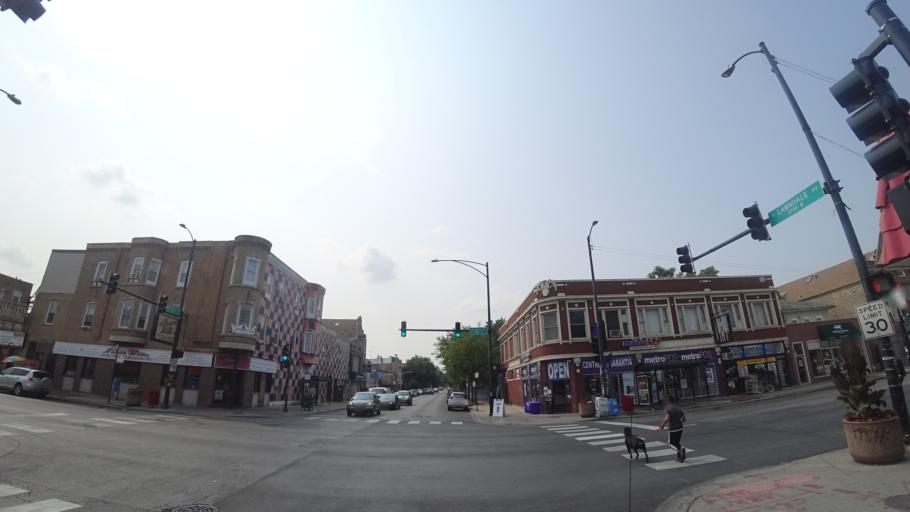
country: US
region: Illinois
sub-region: Cook County
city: Cicero
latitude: 41.8445
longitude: -87.7173
